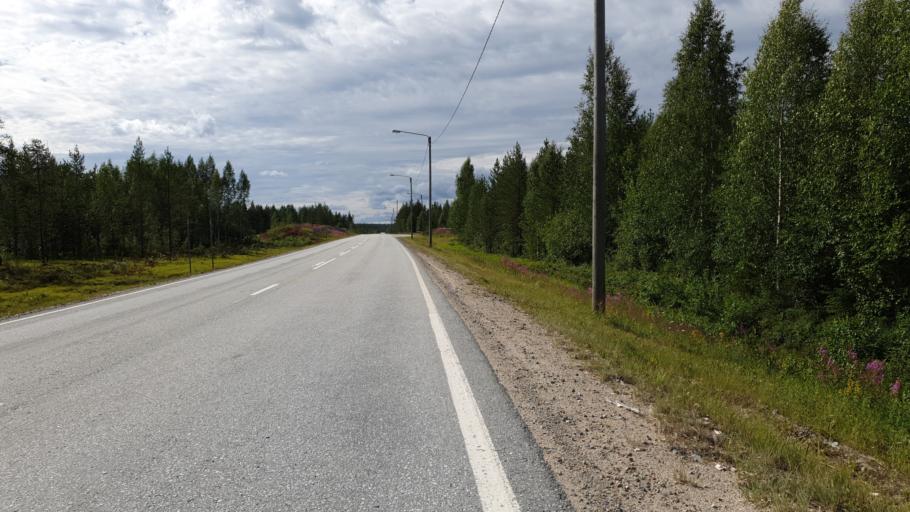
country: FI
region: Kainuu
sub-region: Kehys-Kainuu
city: Kuhmo
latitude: 64.5343
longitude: 29.9440
